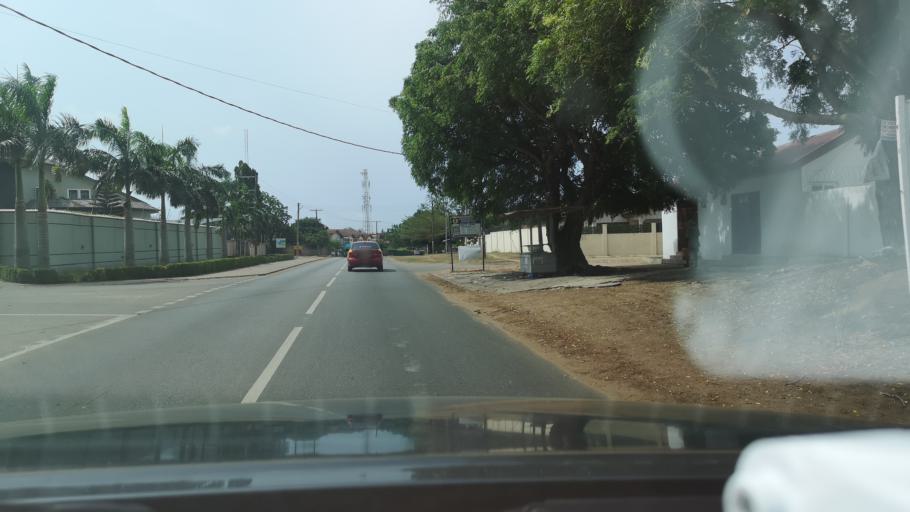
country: GH
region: Greater Accra
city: Tema
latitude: 5.6601
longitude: -0.0251
